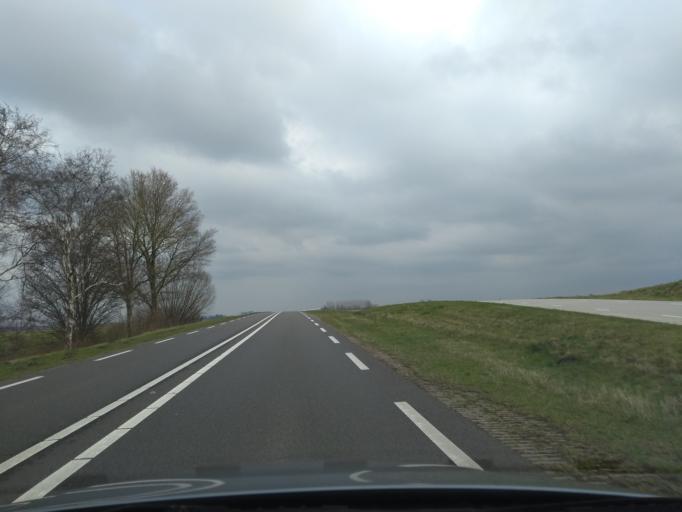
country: NL
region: Overijssel
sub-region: Gemeente Steenwijkerland
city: Sint Jansklooster
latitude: 52.6495
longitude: 6.0161
